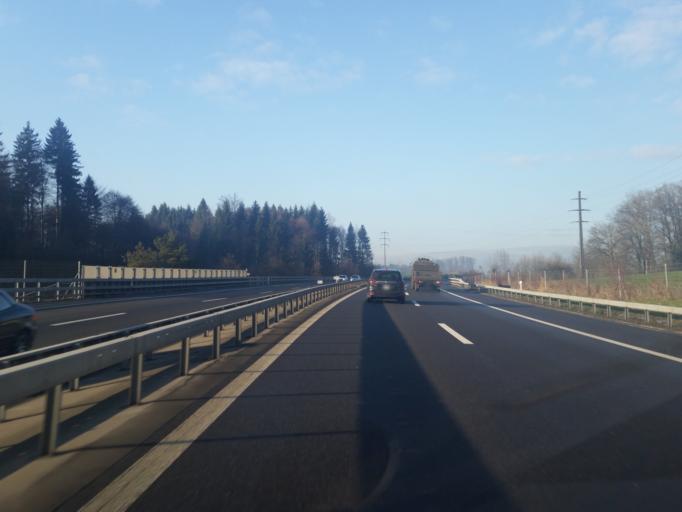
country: CH
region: Zurich
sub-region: Bezirk Affoltern
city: Knonau
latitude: 47.2296
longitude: 8.4606
